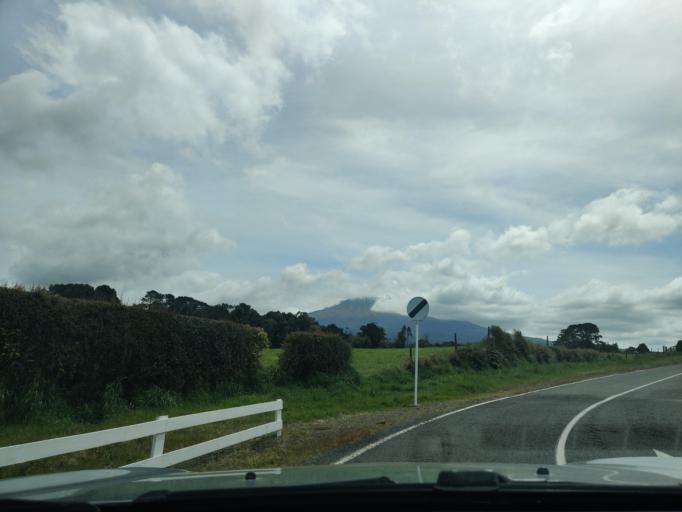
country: NZ
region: Taranaki
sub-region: South Taranaki District
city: Eltham
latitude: -39.3859
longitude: 174.1453
